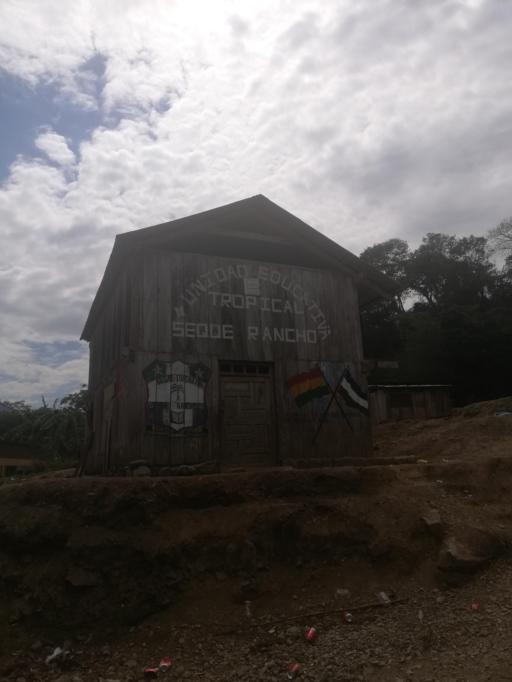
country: BO
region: La Paz
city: Quime
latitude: -16.4751
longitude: -66.7845
